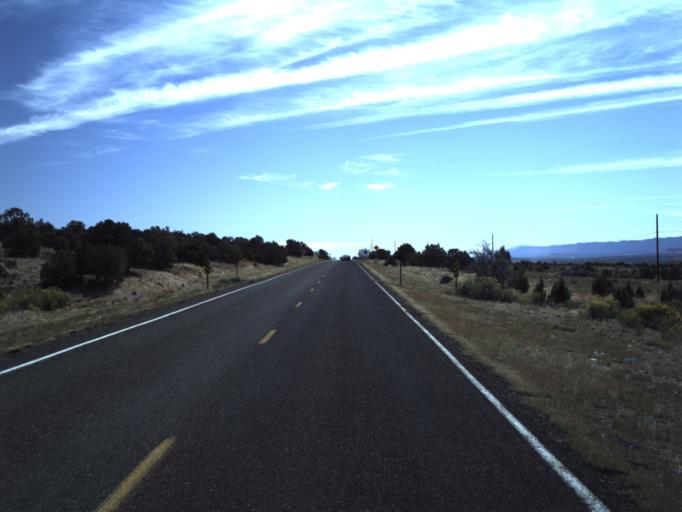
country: US
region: Utah
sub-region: Wayne County
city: Loa
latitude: 37.7325
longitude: -111.5391
